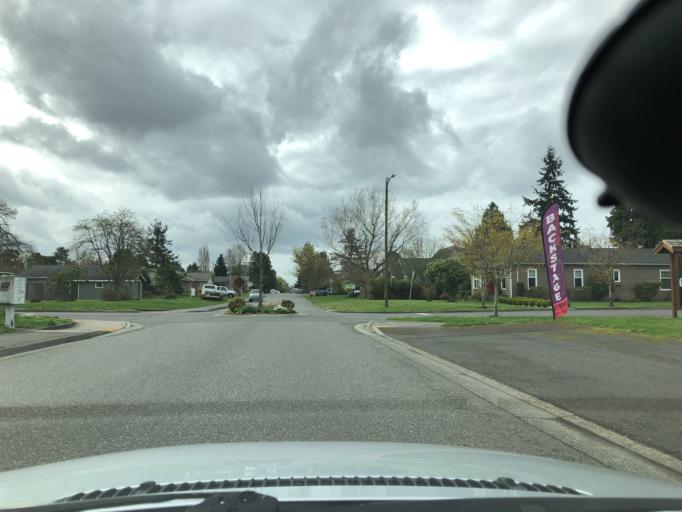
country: US
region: Washington
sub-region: Whatcom County
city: Blaine
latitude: 48.9910
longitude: -122.7481
